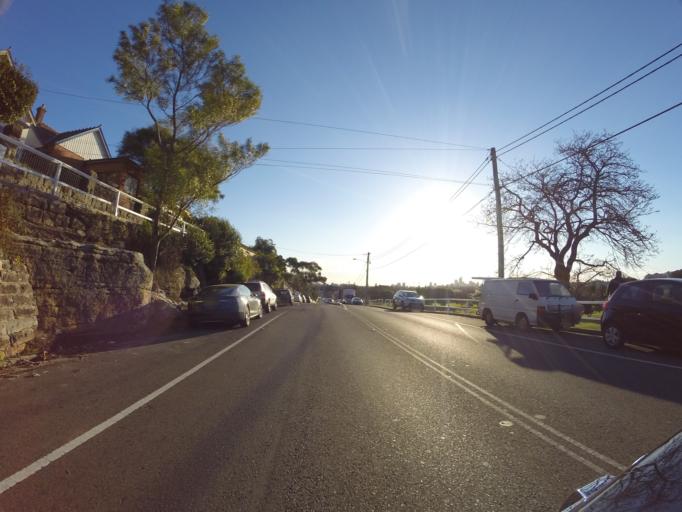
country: AU
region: New South Wales
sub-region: Randwick
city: Randwick
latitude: -33.9037
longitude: 151.2507
